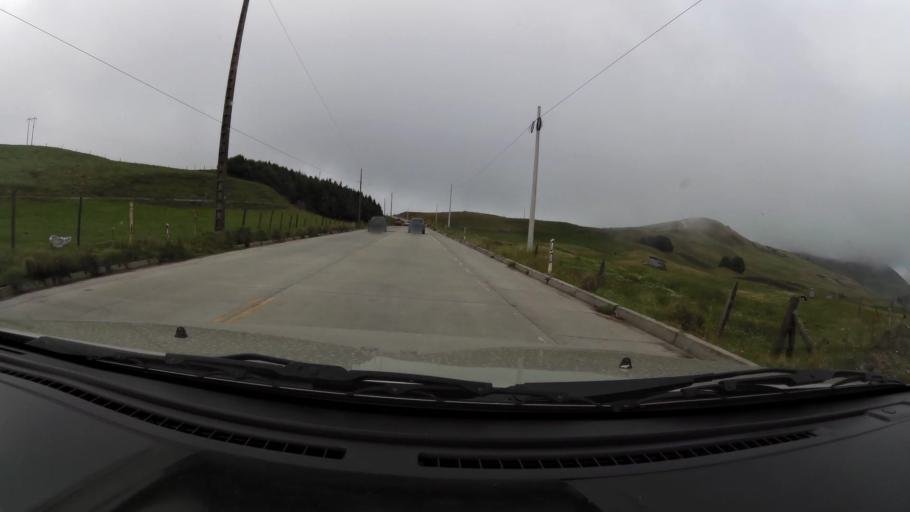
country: EC
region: Canar
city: Canar
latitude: -2.5952
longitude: -78.9173
